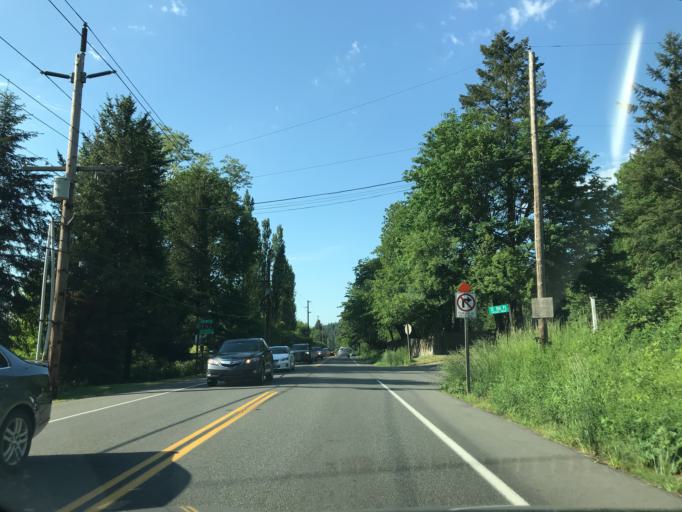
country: US
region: Washington
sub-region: King County
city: Issaquah
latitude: 47.5066
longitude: -122.0228
